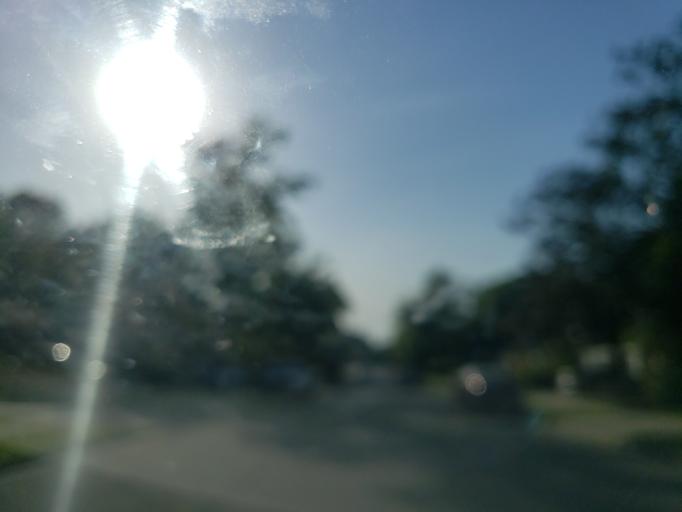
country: US
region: Georgia
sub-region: Chatham County
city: Thunderbolt
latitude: 32.0387
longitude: -81.0870
